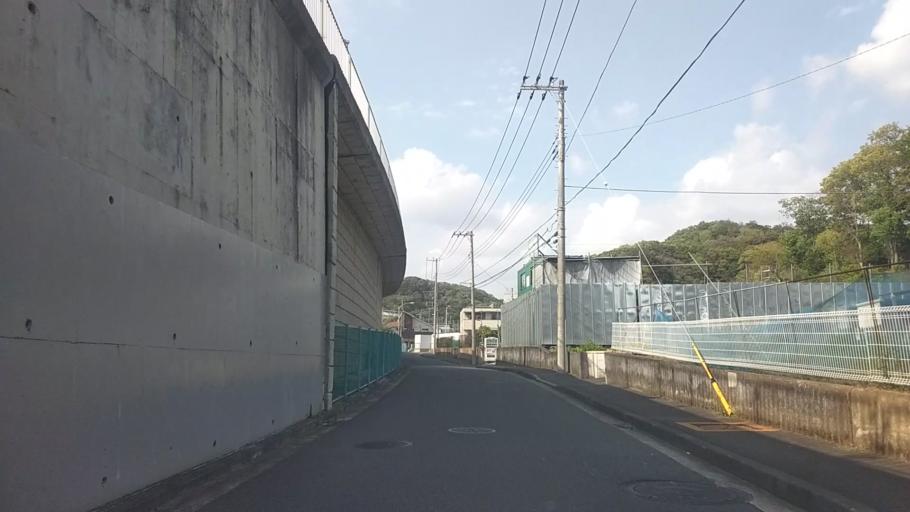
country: JP
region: Kanagawa
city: Kamakura
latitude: 35.3795
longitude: 139.5534
